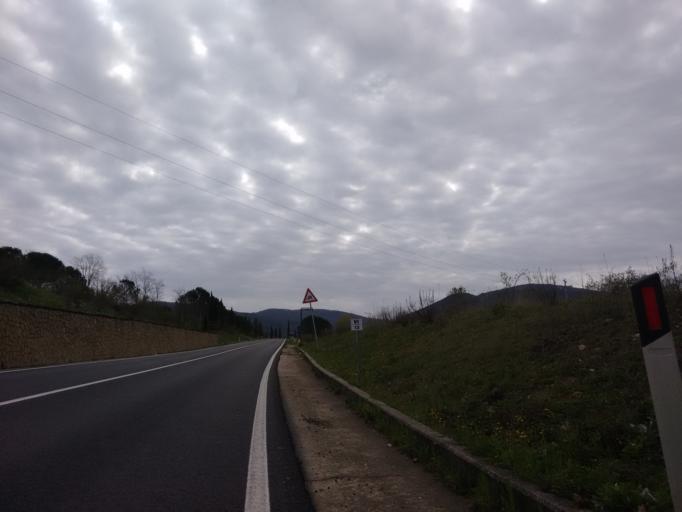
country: IT
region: Tuscany
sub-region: Province of Florence
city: Strada in Chianti
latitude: 43.6534
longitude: 11.3045
